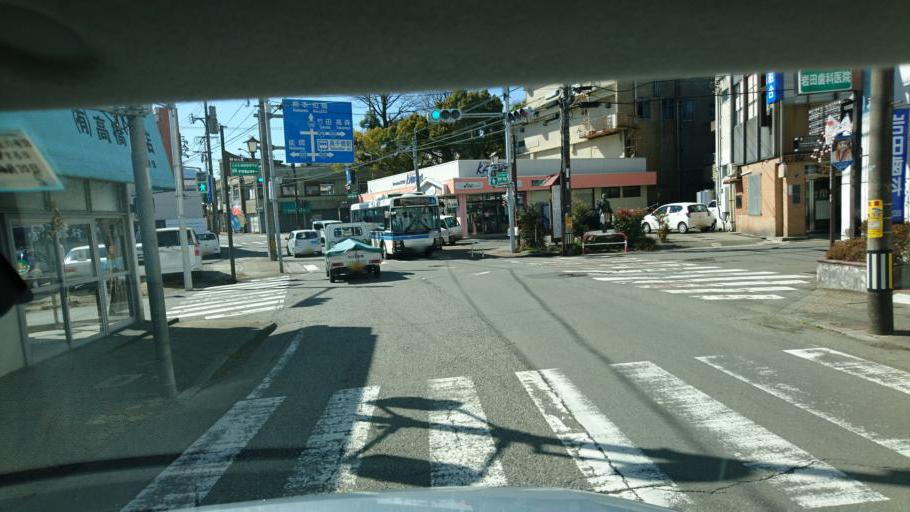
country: JP
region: Oita
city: Takedamachi
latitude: 32.7109
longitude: 131.3091
